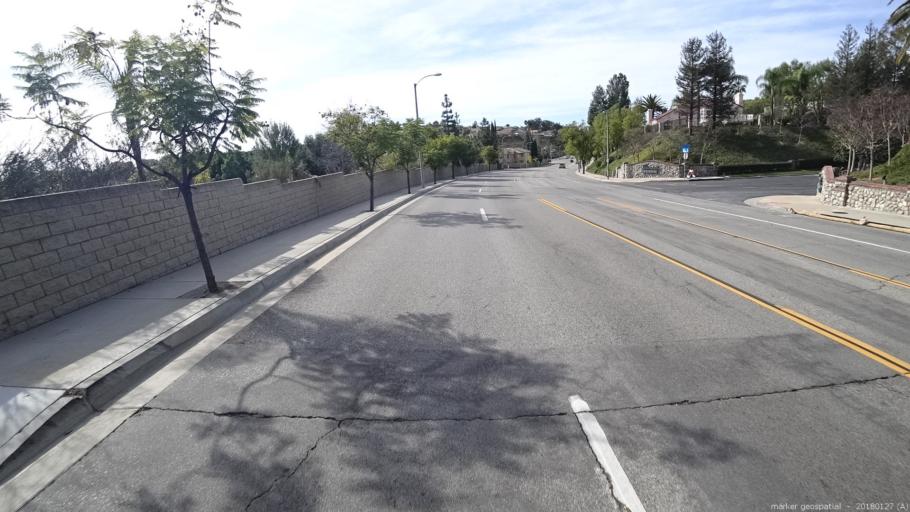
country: US
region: California
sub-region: Los Angeles County
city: Walnut
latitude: 33.9764
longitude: -117.8560
